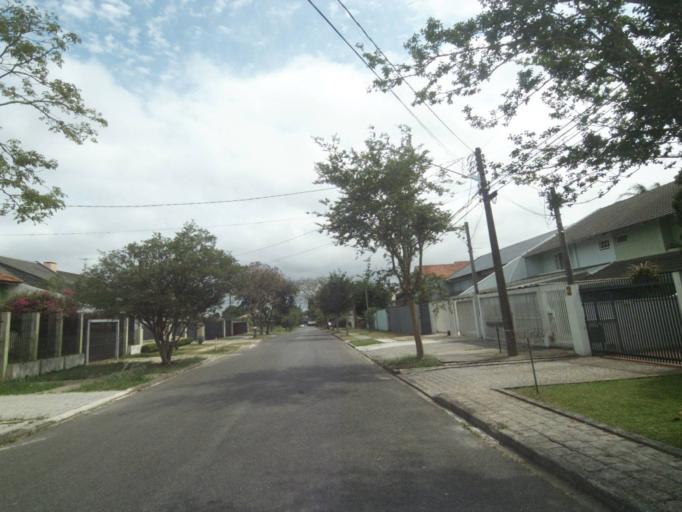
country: BR
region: Parana
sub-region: Pinhais
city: Pinhais
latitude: -25.4322
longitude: -49.2268
